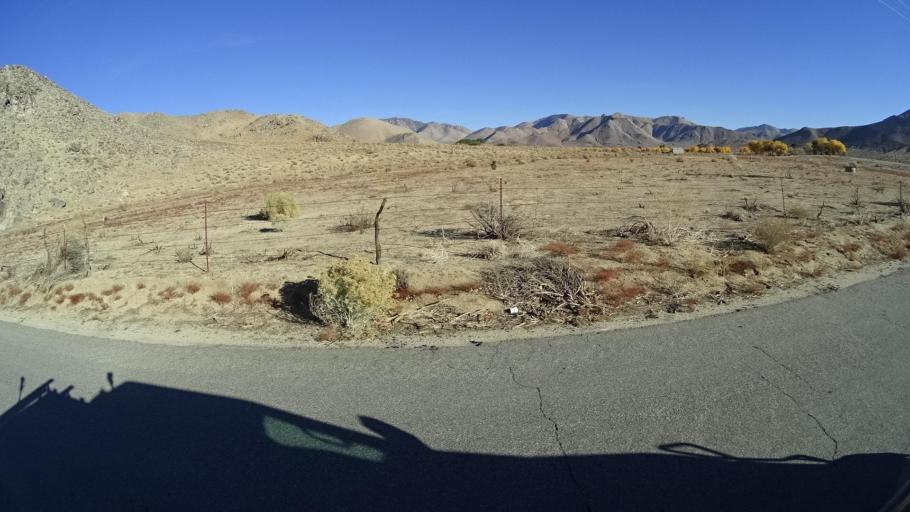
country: US
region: California
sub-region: Kern County
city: Weldon
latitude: 35.5610
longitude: -118.2370
